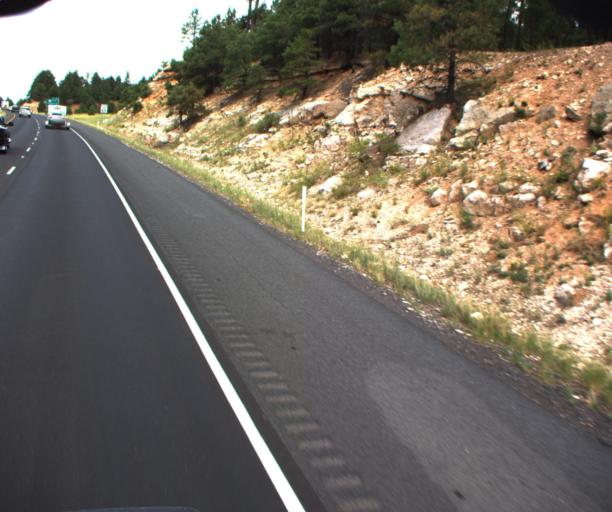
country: US
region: Arizona
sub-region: Coconino County
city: Kachina Village
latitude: 35.1244
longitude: -111.6814
